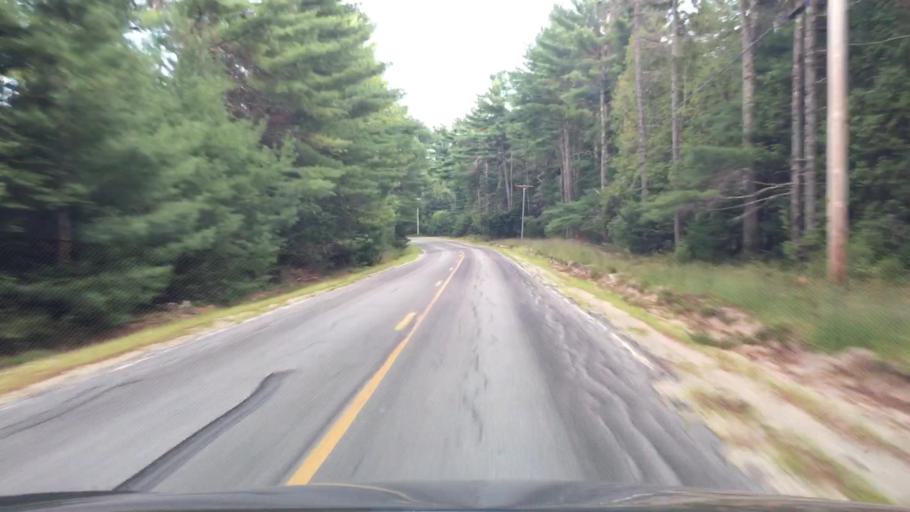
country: US
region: Maine
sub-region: Hancock County
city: Surry
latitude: 44.5087
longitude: -68.5973
